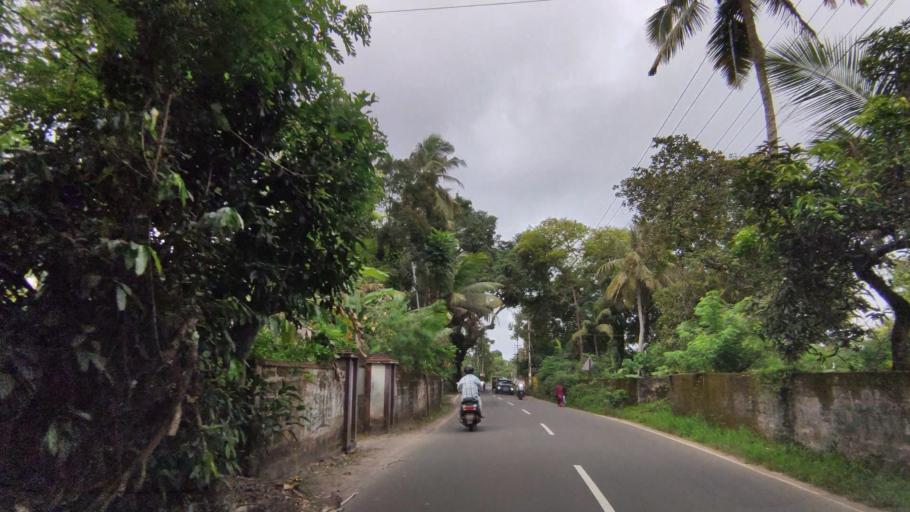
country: IN
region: Kerala
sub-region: Alappuzha
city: Shertallai
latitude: 9.6021
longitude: 76.3586
